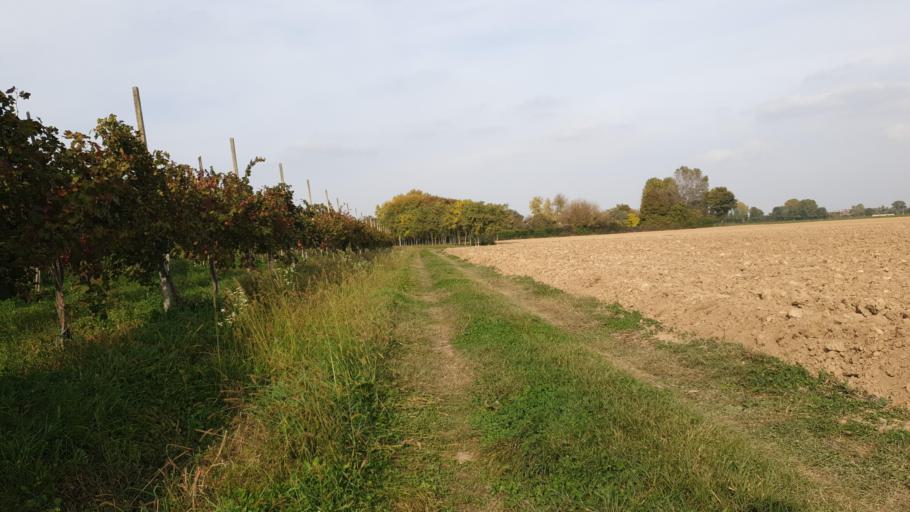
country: IT
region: Veneto
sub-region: Provincia di Padova
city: Casalserugo
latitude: 45.3391
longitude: 11.9181
